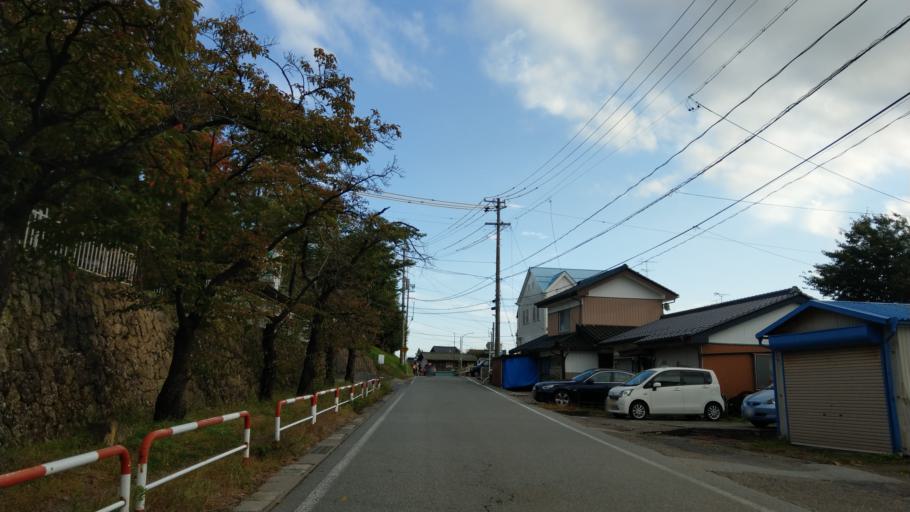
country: JP
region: Nagano
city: Komoro
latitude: 36.3345
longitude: 138.4198
